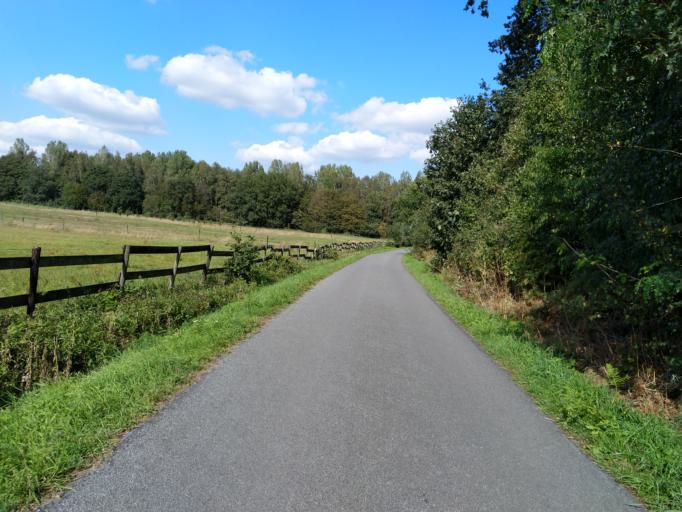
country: BE
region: Wallonia
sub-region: Province du Hainaut
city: Saint-Ghislain
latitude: 50.4986
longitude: 3.8129
